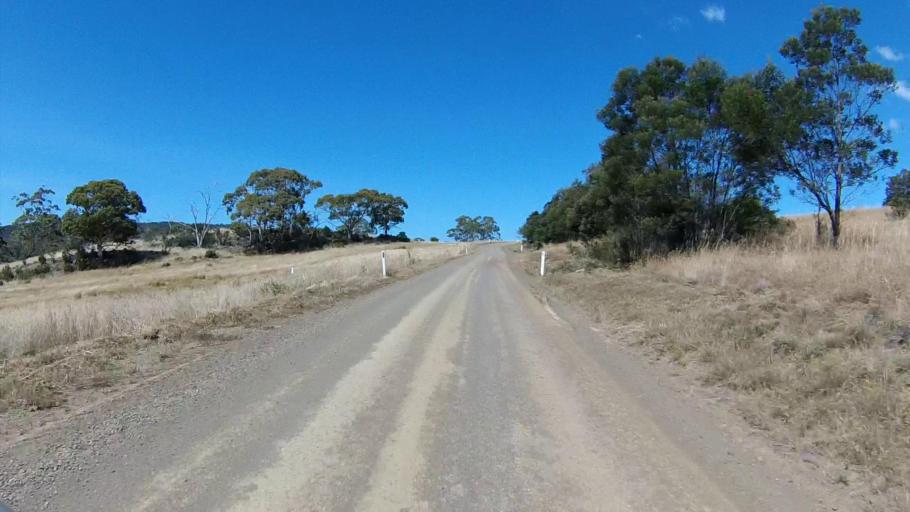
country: AU
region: Tasmania
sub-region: Break O'Day
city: St Helens
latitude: -41.9661
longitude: 148.0743
